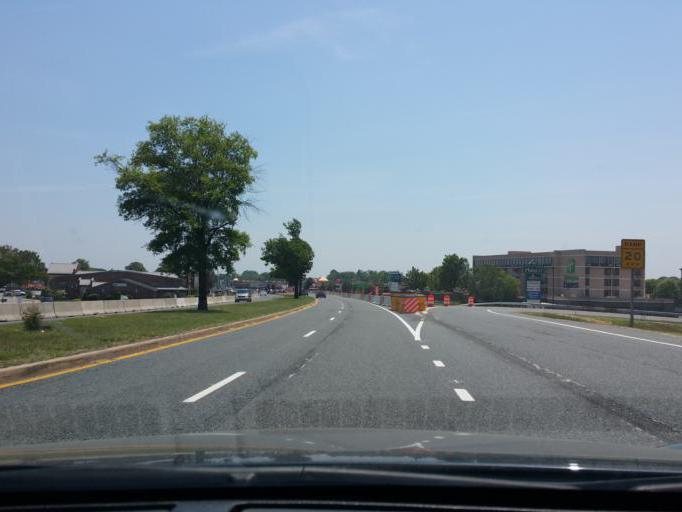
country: US
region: Maryland
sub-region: Harford County
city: Aberdeen
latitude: 39.5241
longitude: -76.1877
